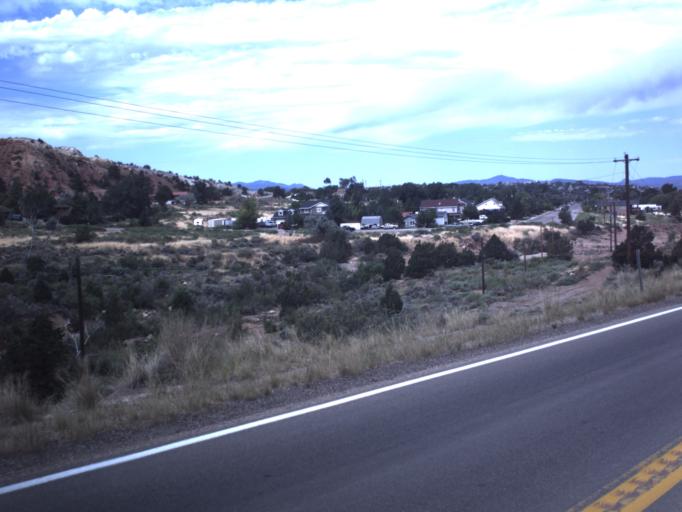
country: US
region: Utah
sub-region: Iron County
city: Cedar City
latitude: 37.6741
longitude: -113.0461
